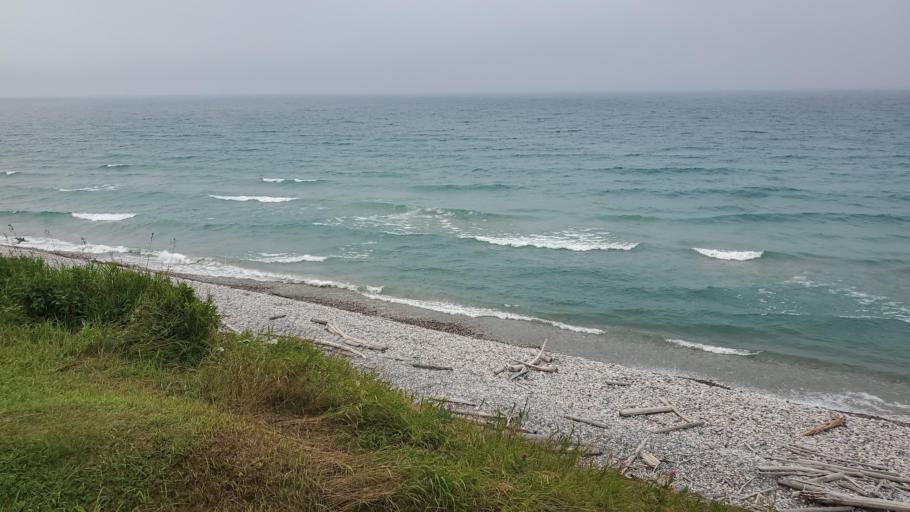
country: CA
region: Ontario
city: Marathon
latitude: 48.7070
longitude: -86.3868
